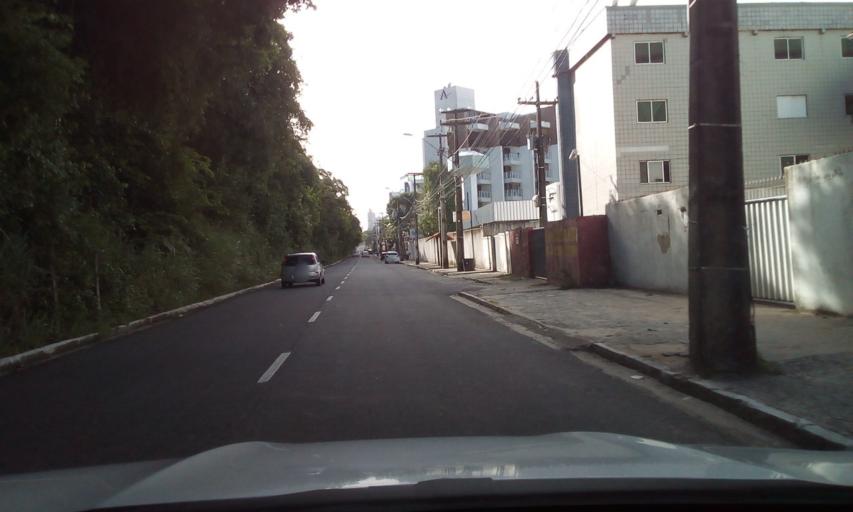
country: BR
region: Paraiba
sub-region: Joao Pessoa
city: Joao Pessoa
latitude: -7.1356
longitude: -34.8215
